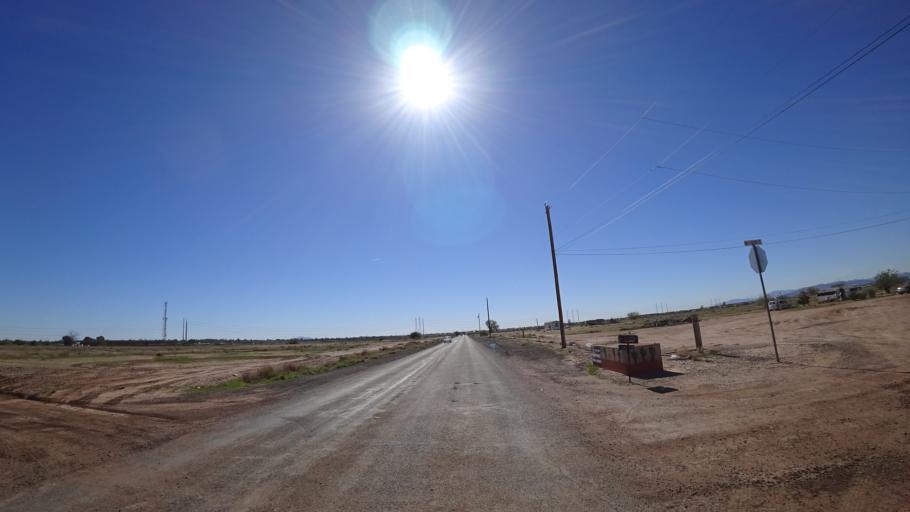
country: US
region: Arizona
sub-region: Maricopa County
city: Mesa
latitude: 33.4587
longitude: -111.8660
